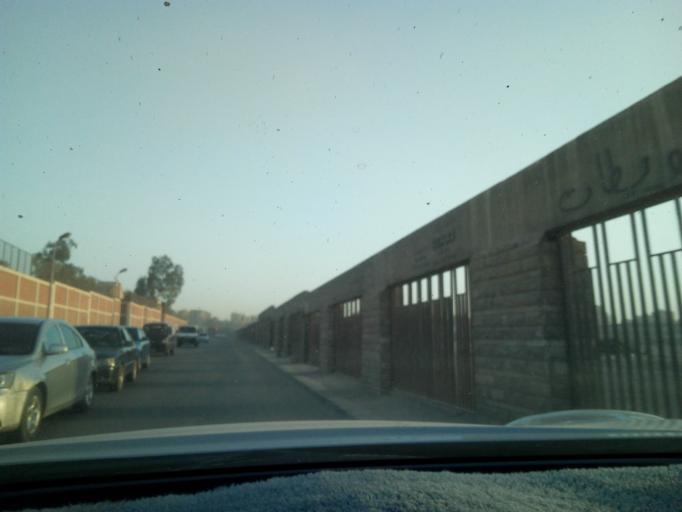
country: EG
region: Muhafazat al Qalyubiyah
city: Al Khankah
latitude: 30.1260
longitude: 31.3555
